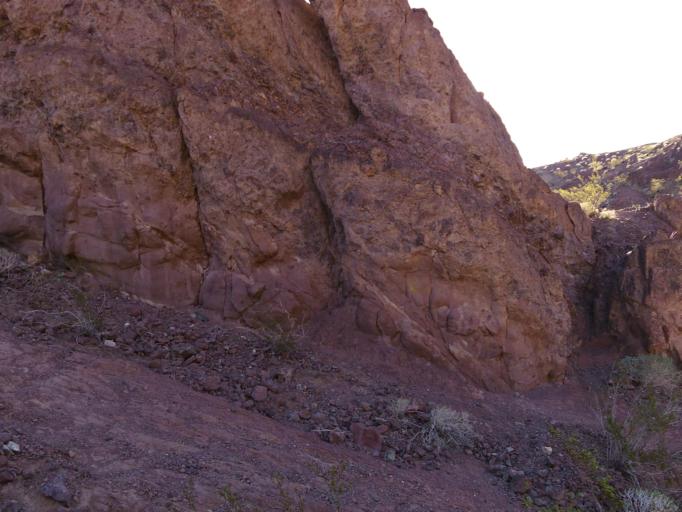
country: US
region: Nevada
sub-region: Clark County
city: Boulder City
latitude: 35.9613
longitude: -114.7283
